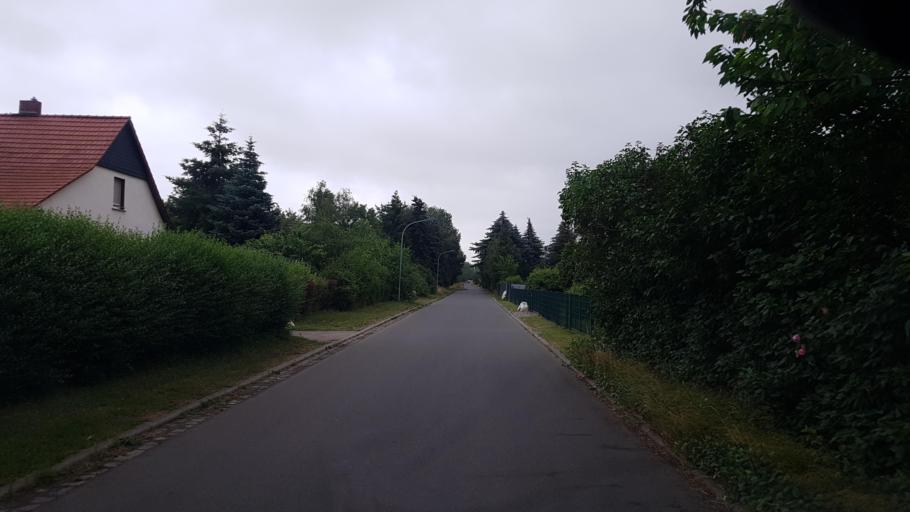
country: DE
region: Brandenburg
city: Juterbog
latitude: 51.9122
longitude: 13.1931
